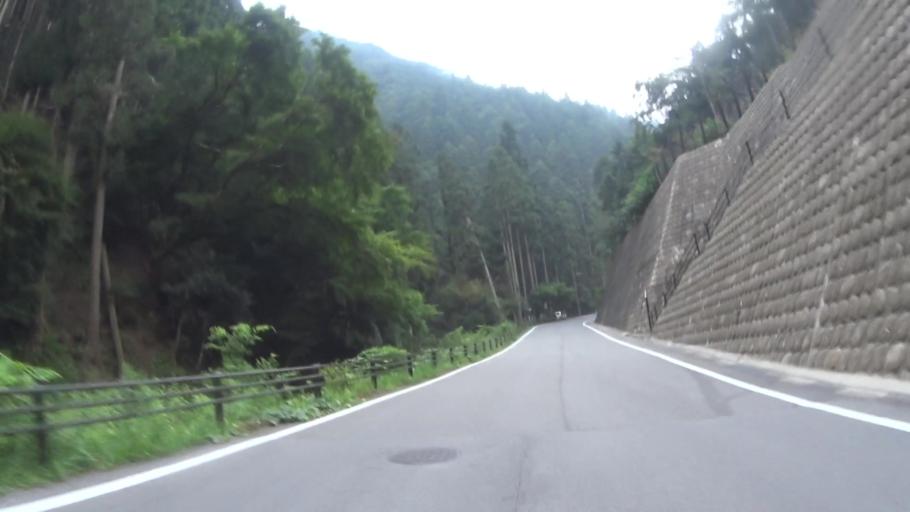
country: JP
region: Kyoto
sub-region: Kyoto-shi
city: Kamigyo-ku
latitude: 35.1096
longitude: 135.7612
